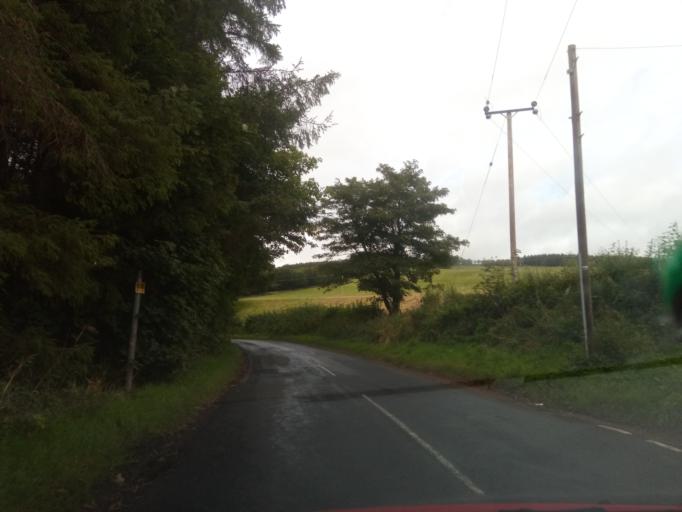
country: GB
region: Scotland
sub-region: The Scottish Borders
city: Duns
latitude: 55.8178
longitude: -2.3931
